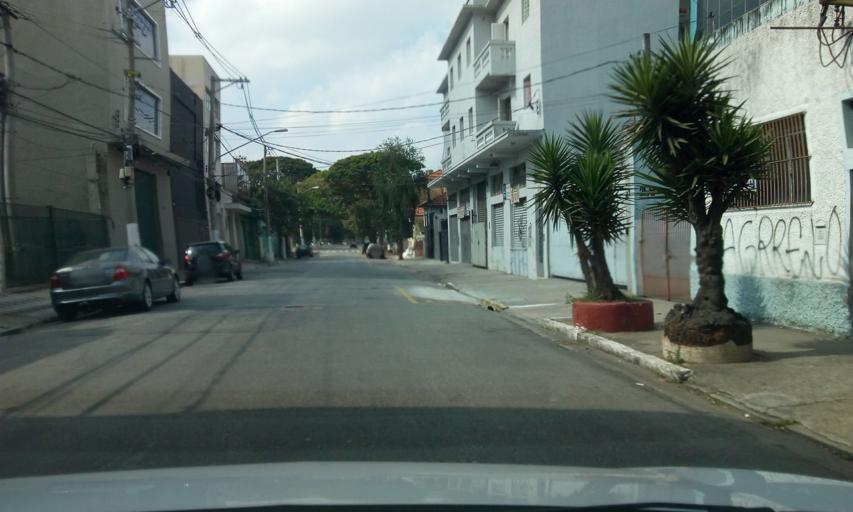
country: BR
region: Sao Paulo
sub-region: Sao Paulo
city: Sao Paulo
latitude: -23.5217
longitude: -46.6445
